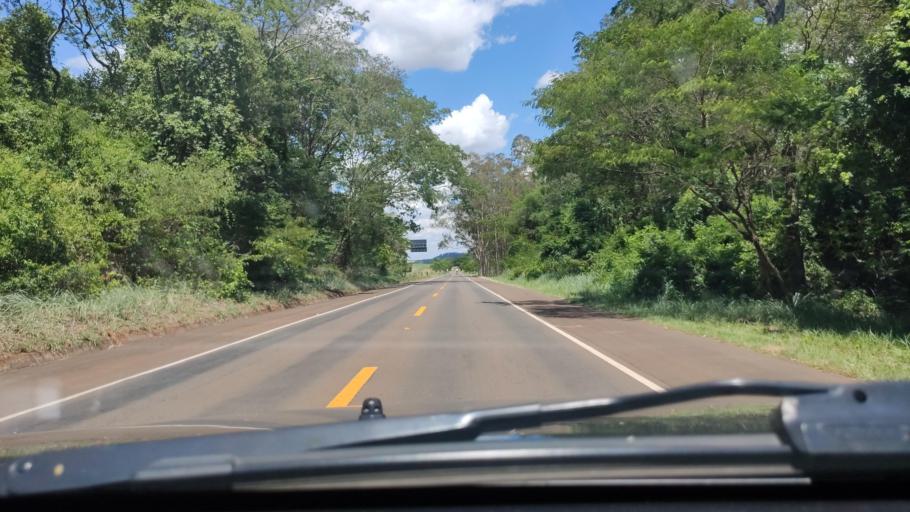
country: BR
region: Sao Paulo
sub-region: Boa Esperanca Do Sul
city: Boa Esperanca do Sul
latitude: -22.0698
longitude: -48.4209
